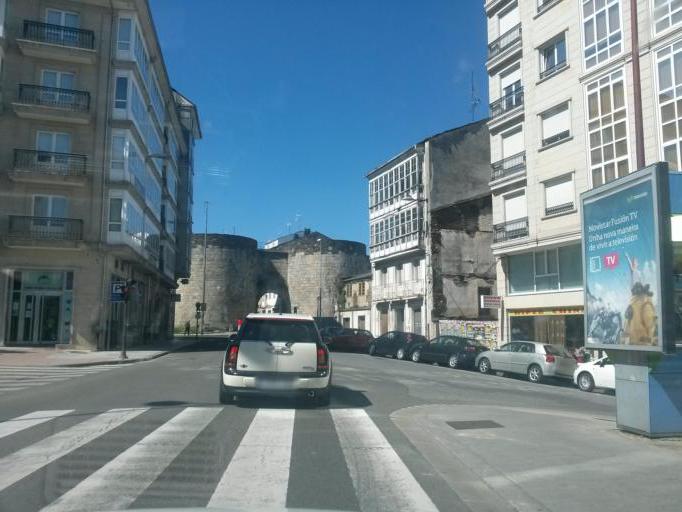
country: ES
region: Galicia
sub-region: Provincia de Lugo
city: Lugo
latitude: 43.0099
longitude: -7.5525
